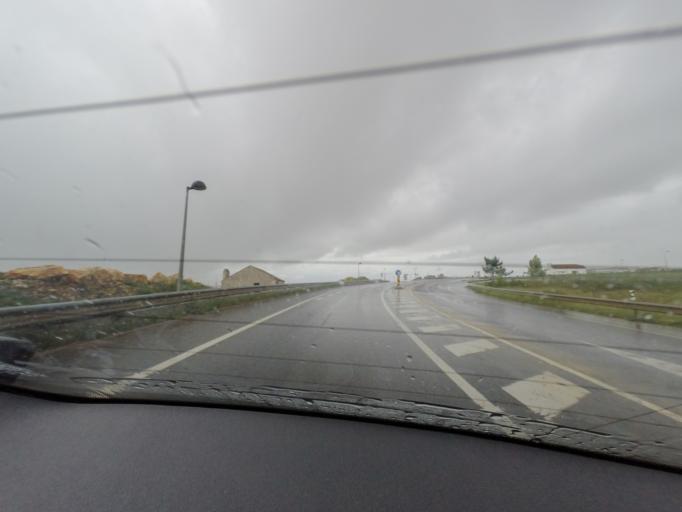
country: PT
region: Lisbon
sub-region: Sintra
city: Pero Pinheiro
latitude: 38.8413
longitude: -9.3496
